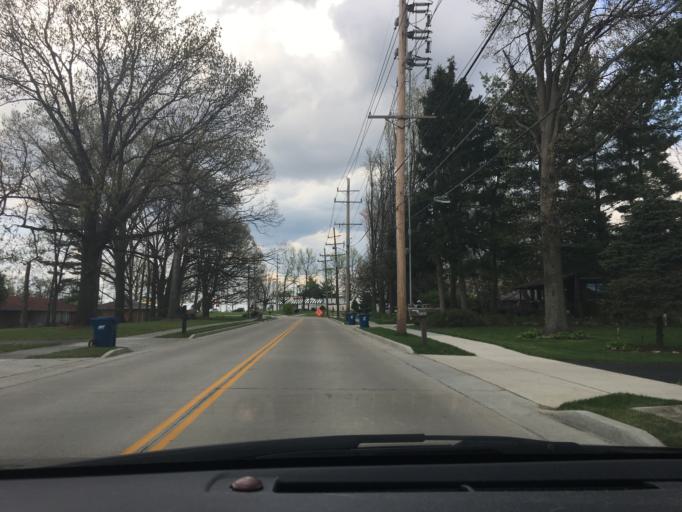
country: US
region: Missouri
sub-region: Saint Louis County
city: Saint Ann
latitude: 38.7299
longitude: -90.4075
